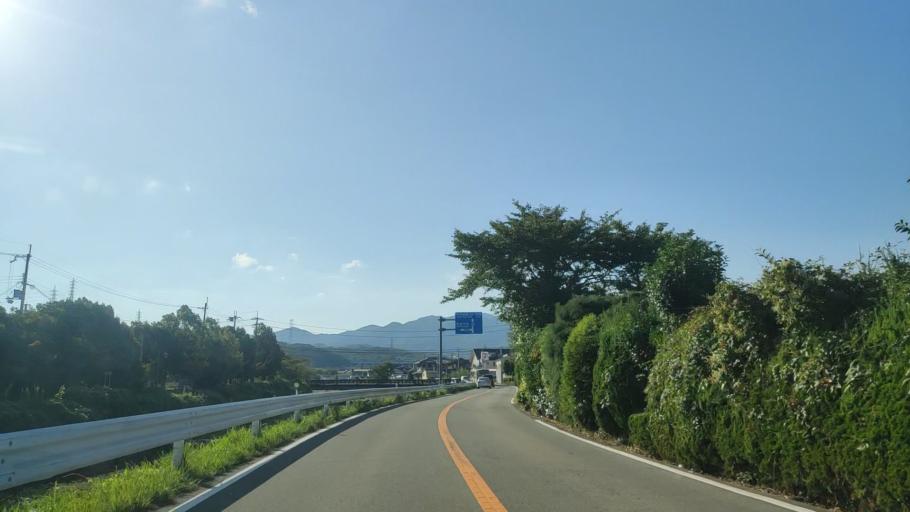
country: JP
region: Hyogo
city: Sandacho
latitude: 34.8259
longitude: 135.2434
